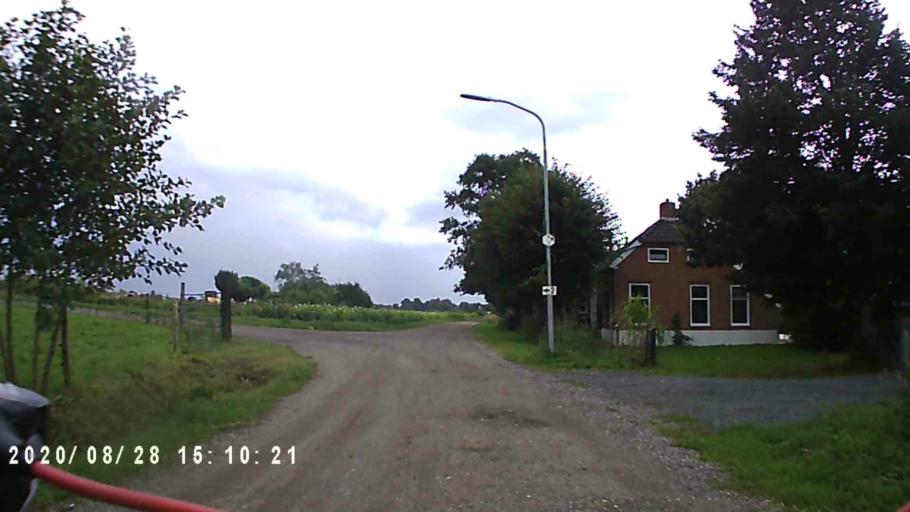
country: NL
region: Groningen
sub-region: Gemeente Haren
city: Haren
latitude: 53.1309
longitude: 6.5703
